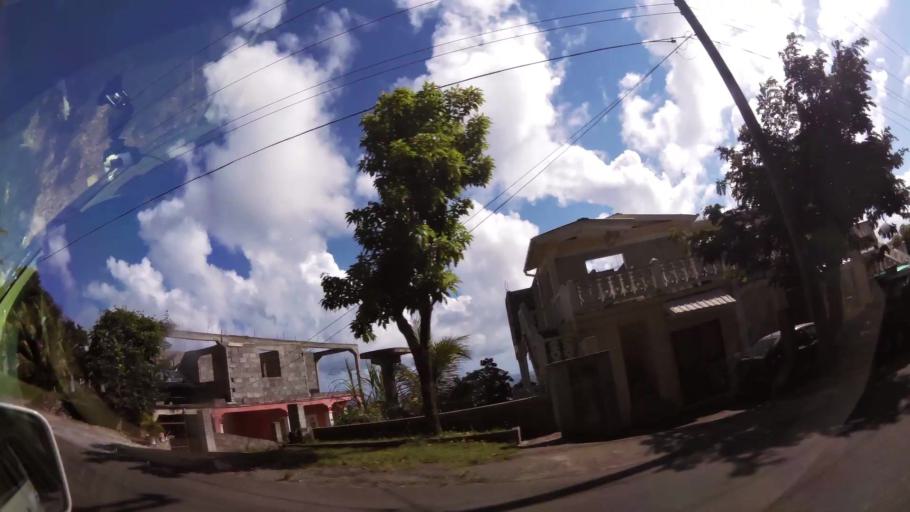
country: VC
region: Saint George
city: Kingstown
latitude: 13.1448
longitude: -61.1665
